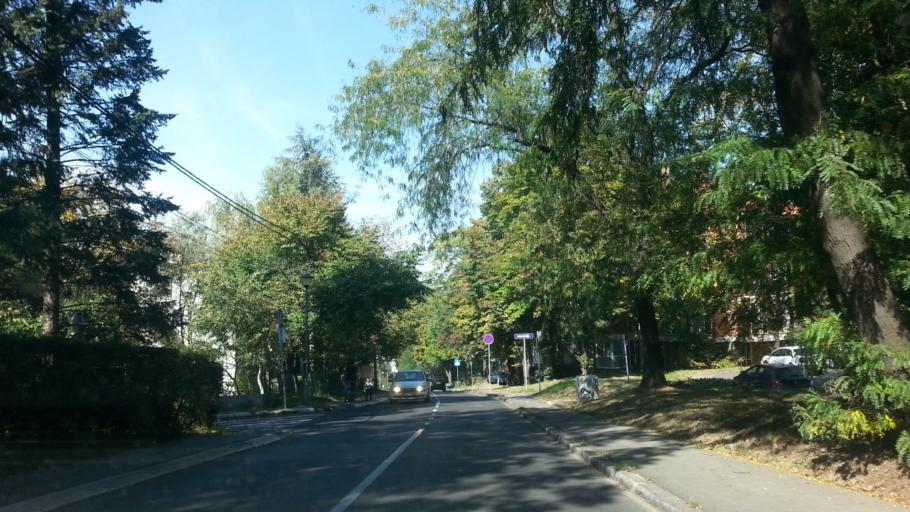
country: RS
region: Central Serbia
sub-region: Belgrade
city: Cukarica
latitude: 44.7769
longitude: 20.4240
